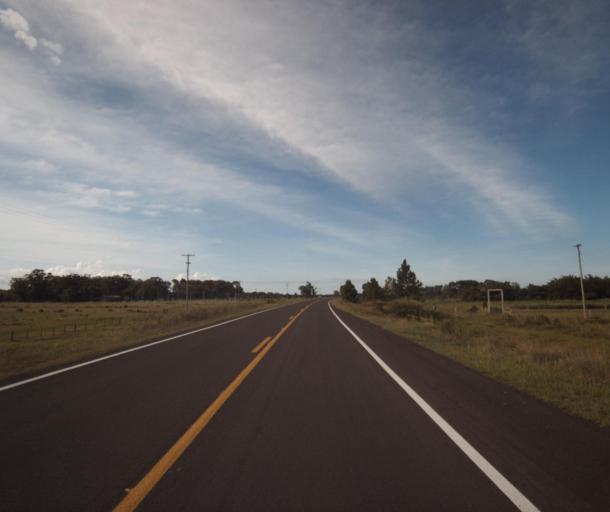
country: BR
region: Rio Grande do Sul
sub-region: Tapes
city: Tapes
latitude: -31.3229
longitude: -51.1244
